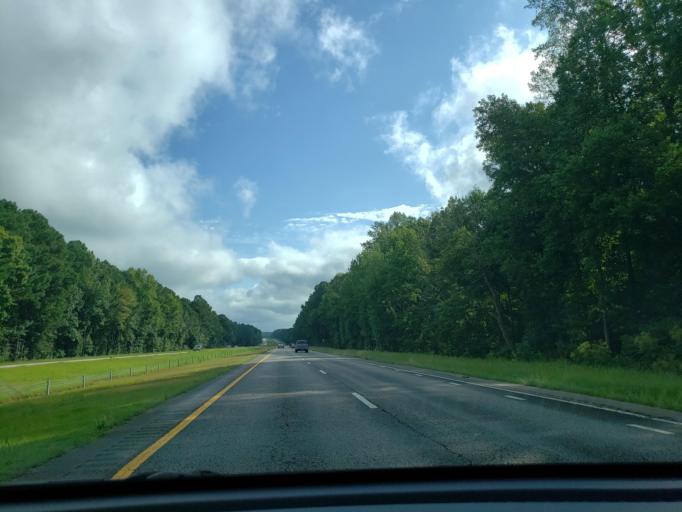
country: US
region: North Carolina
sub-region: Wake County
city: Zebulon
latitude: 35.8388
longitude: -78.2992
